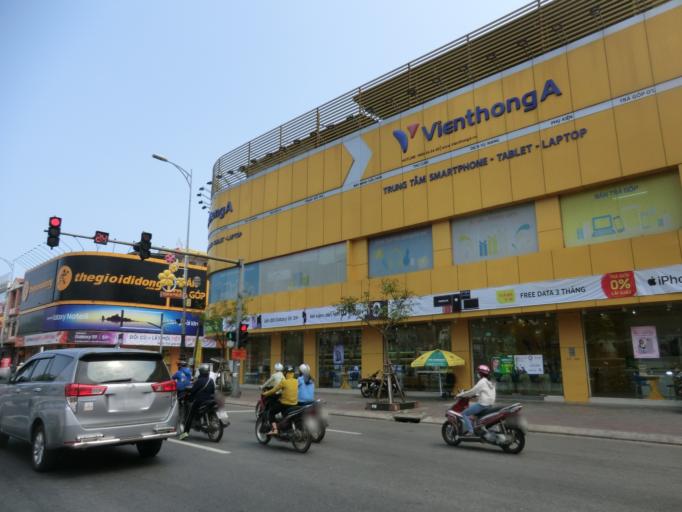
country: VN
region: Da Nang
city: Thanh Khe
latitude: 16.0657
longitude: 108.1917
